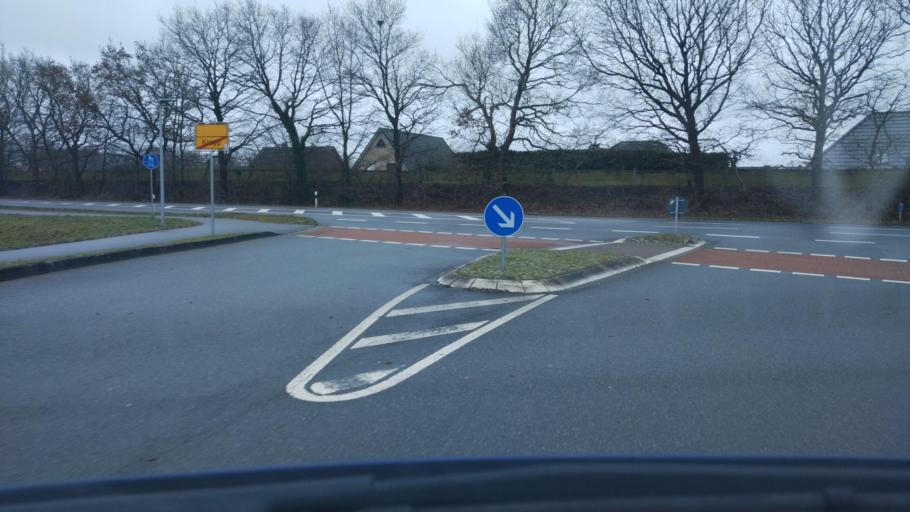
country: DE
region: Schleswig-Holstein
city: Kropp
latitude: 54.4171
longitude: 9.4965
